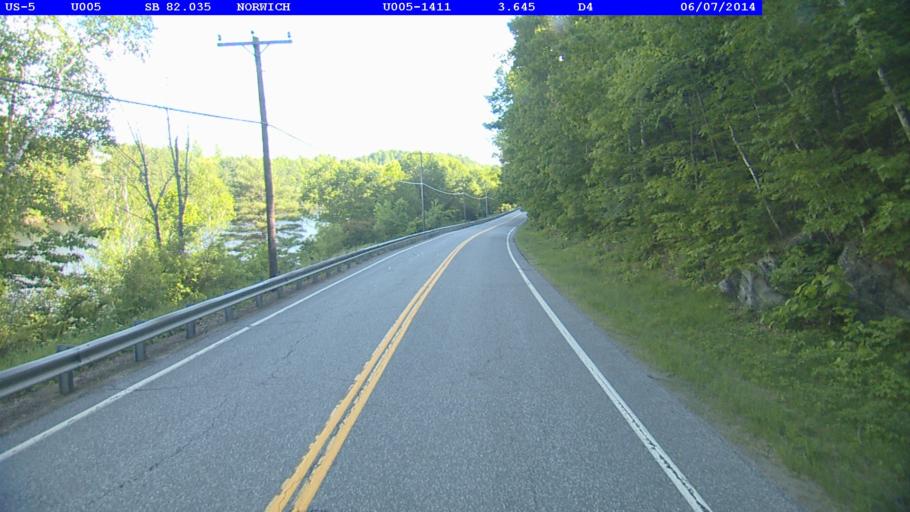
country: US
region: New Hampshire
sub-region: Grafton County
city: Hanover
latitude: 43.7309
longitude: -72.2744
